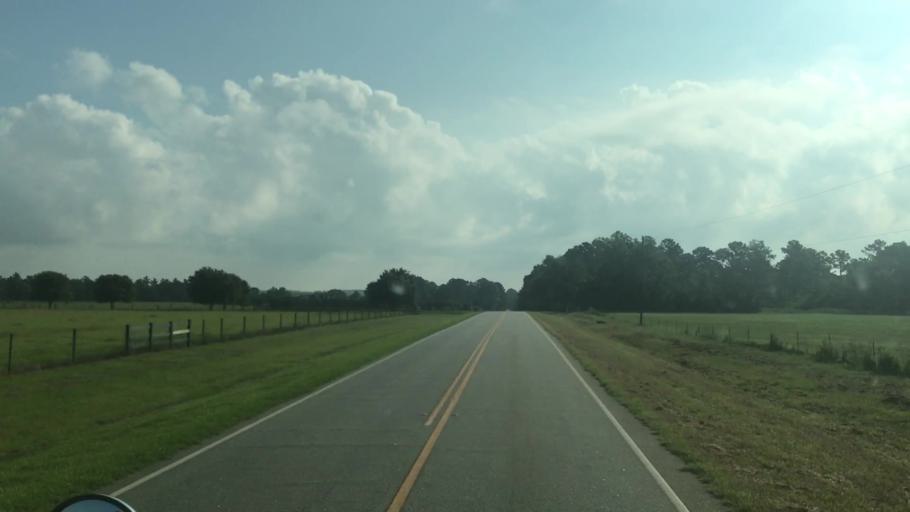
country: US
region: Florida
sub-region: Gadsden County
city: Havana
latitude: 30.7091
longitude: -84.5059
